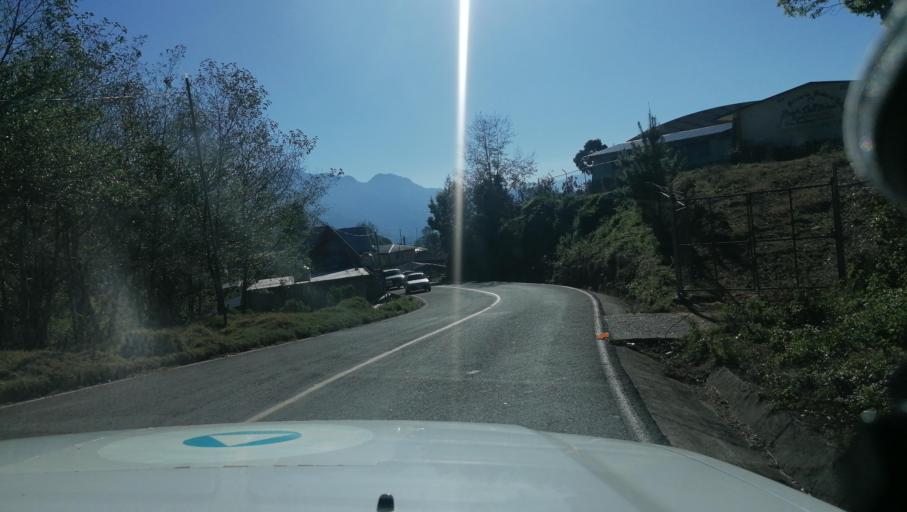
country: MX
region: Chiapas
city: Motozintla de Mendoza
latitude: 15.2479
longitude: -92.2285
